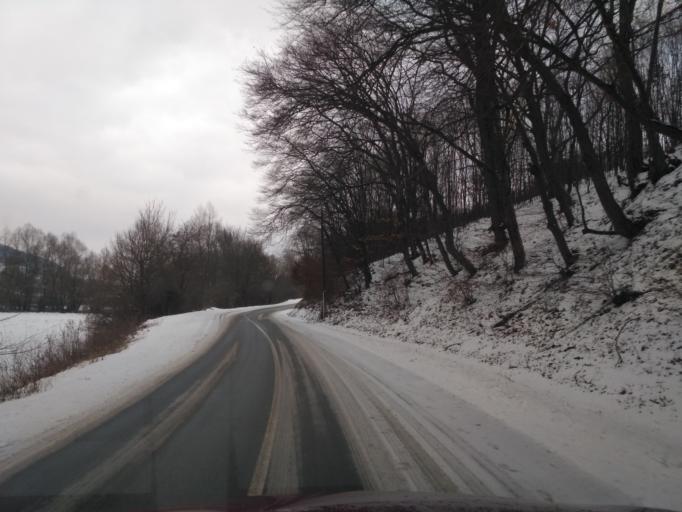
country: SK
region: Presovsky
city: Sabinov
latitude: 49.0322
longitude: 21.1021
